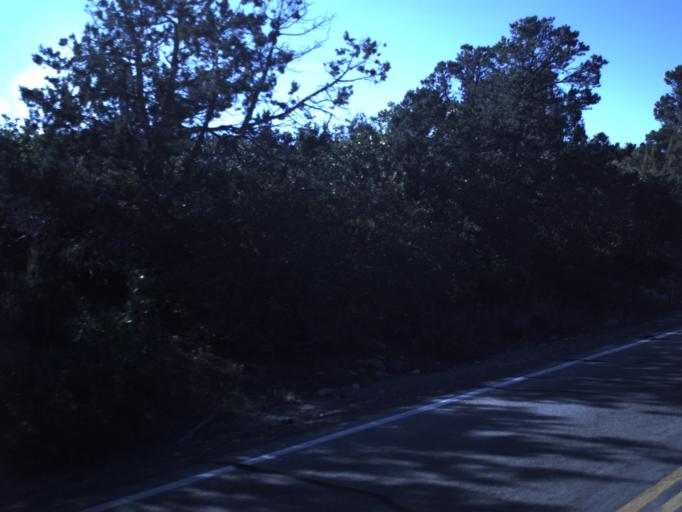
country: US
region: Utah
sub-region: Grand County
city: Moab
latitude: 38.3233
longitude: -109.2256
